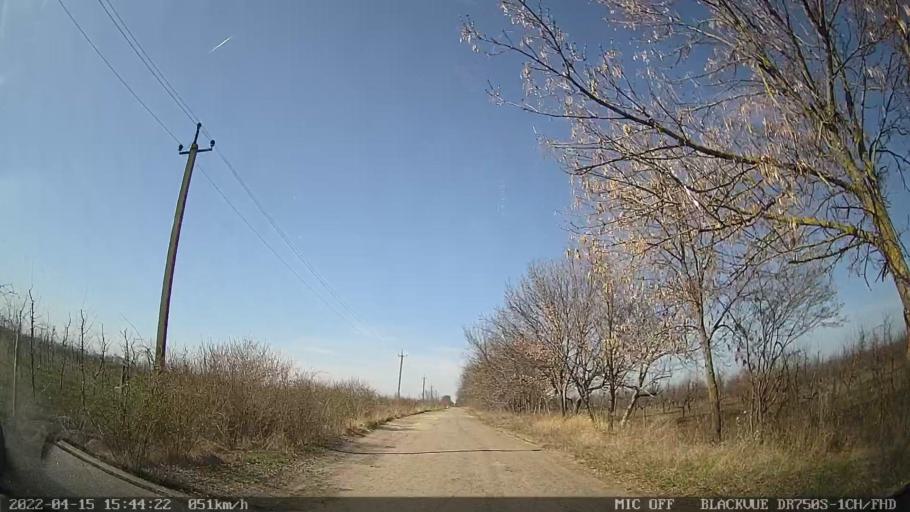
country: MD
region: Raionul Ocnita
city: Otaci
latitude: 48.3701
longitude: 27.9226
